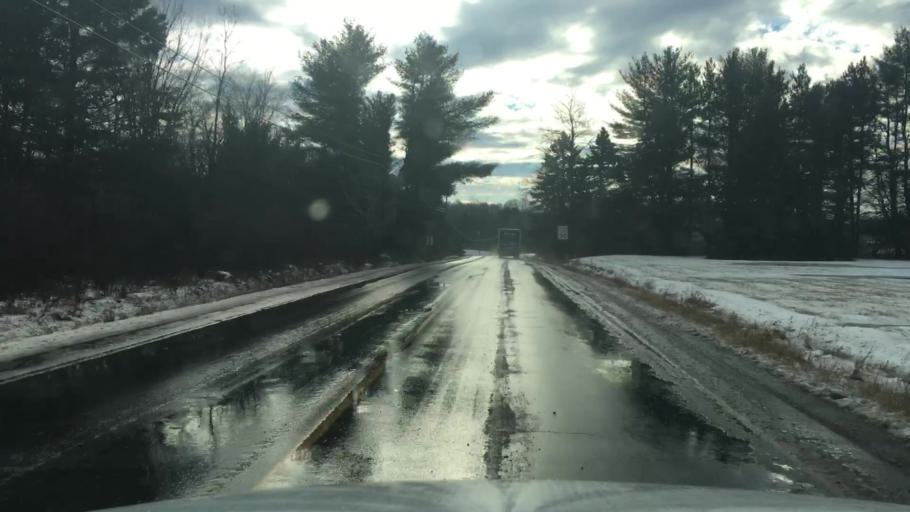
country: US
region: Maine
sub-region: Penobscot County
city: Brewer
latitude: 44.7436
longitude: -68.7657
